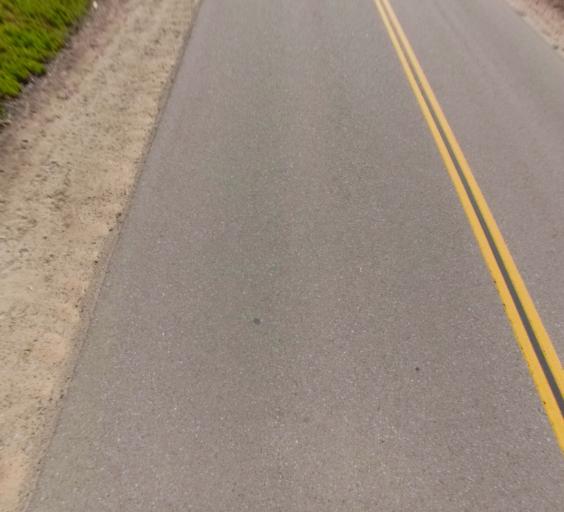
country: US
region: California
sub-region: Madera County
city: Bonadelle Ranchos-Madera Ranchos
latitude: 37.0031
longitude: -119.8855
